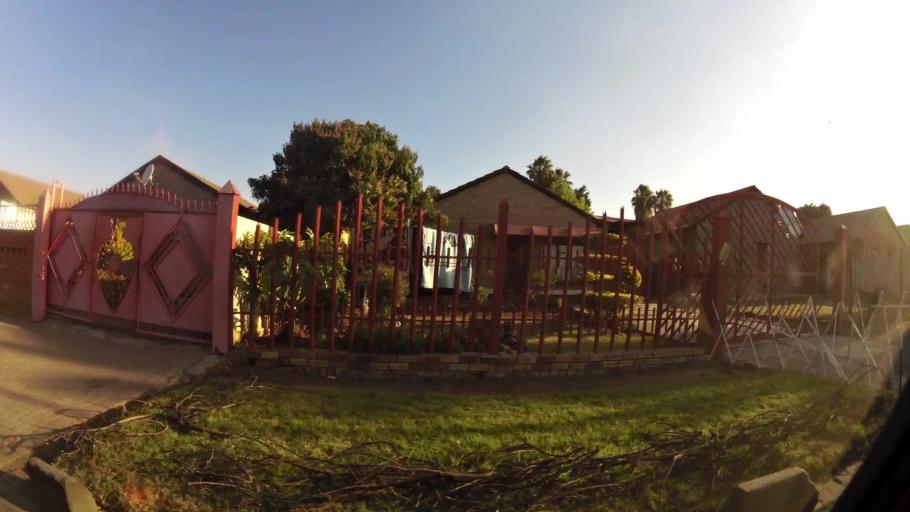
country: ZA
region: North-West
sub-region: Bojanala Platinum District Municipality
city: Rustenburg
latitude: -25.6434
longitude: 27.2268
